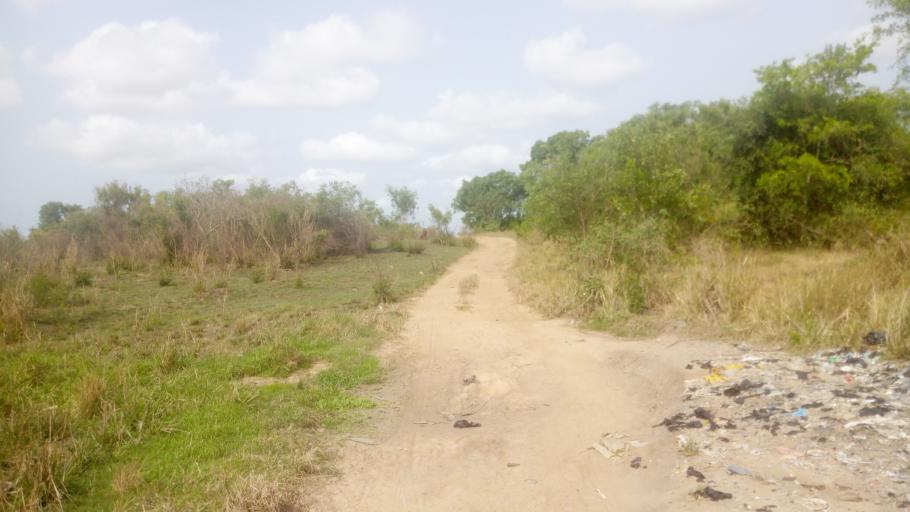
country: GH
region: Central
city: Winneba
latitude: 5.3793
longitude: -0.6265
